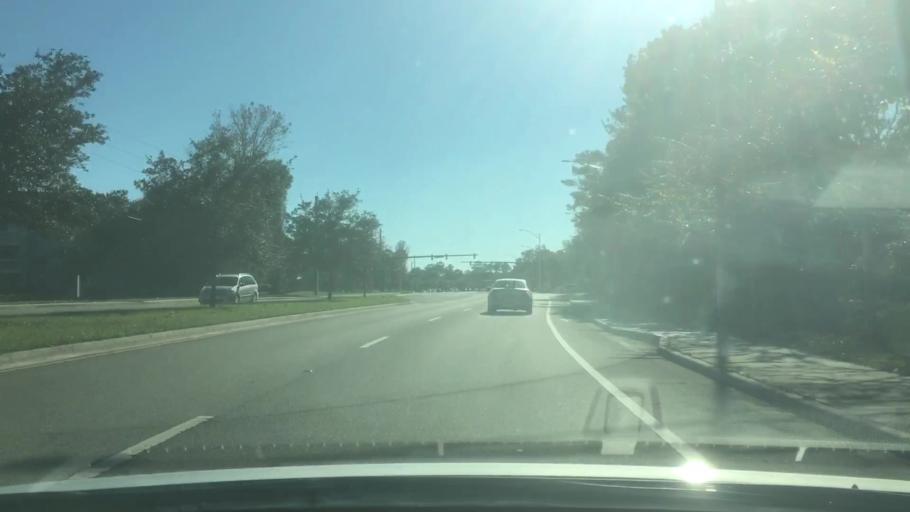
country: US
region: Florida
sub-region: Duval County
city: Neptune Beach
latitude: 30.3144
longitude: -81.4577
